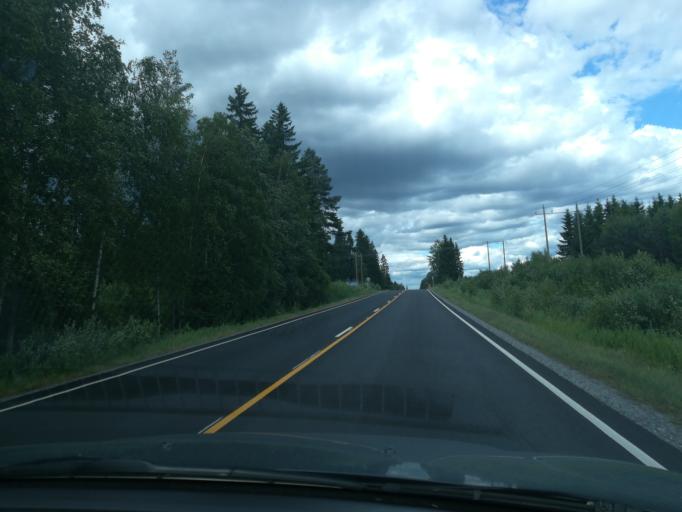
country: FI
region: Southern Savonia
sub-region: Mikkeli
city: Mikkeli
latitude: 61.6502
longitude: 27.0882
